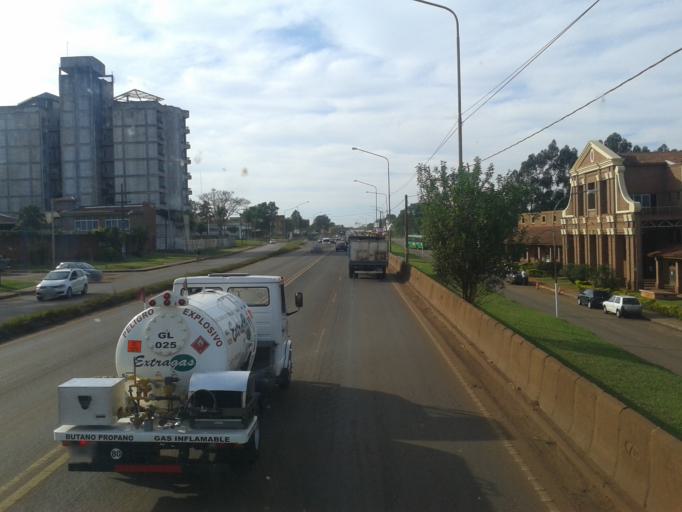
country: AR
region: Misiones
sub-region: Departamento de Capital
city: Posadas
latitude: -27.4315
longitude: -55.8889
